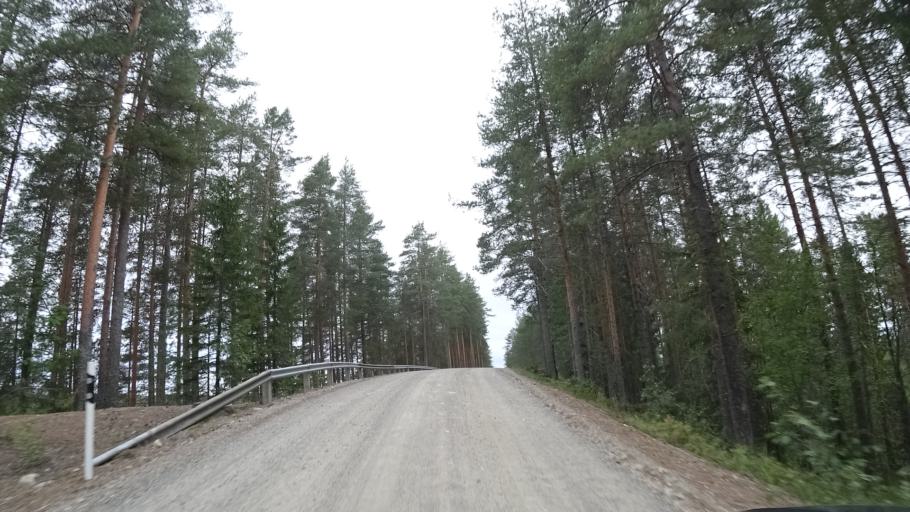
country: FI
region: North Karelia
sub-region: Pielisen Karjala
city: Lieksa
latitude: 63.2329
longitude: 30.3684
